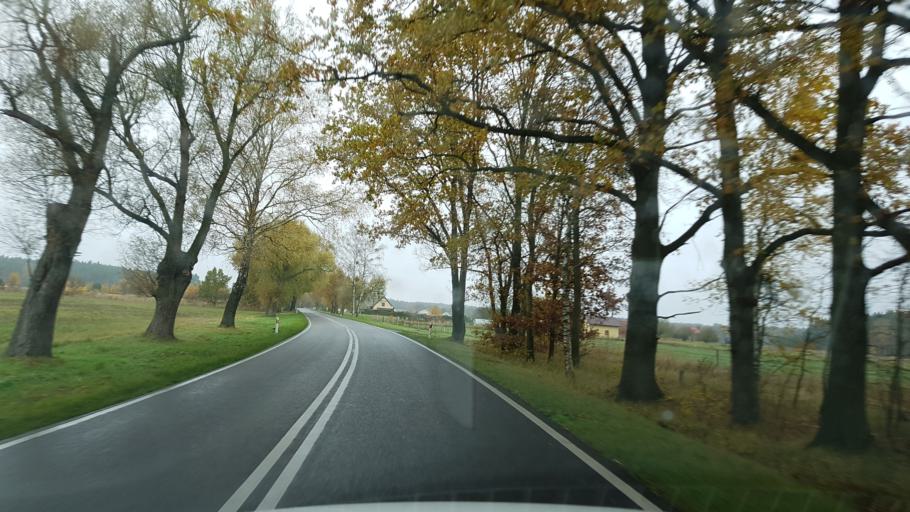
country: PL
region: West Pomeranian Voivodeship
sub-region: Powiat goleniowski
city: Goleniow
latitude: 53.6141
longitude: 14.7418
